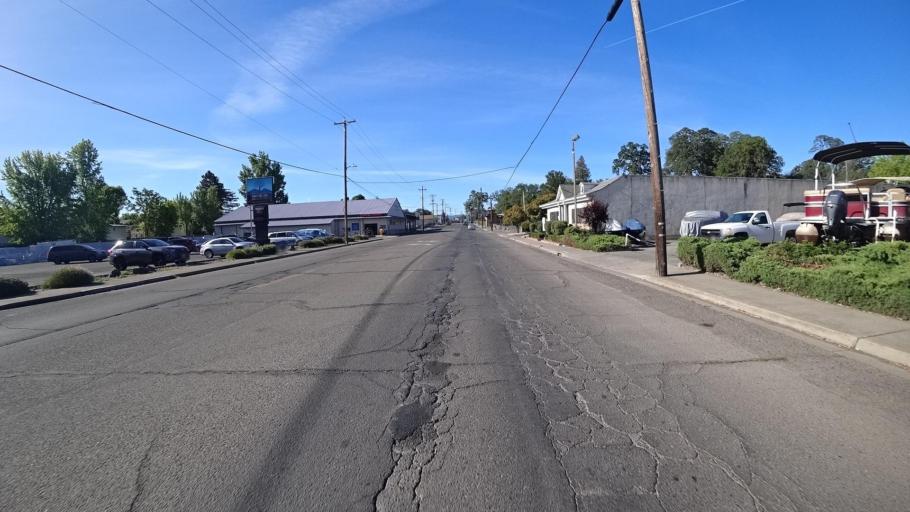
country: US
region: California
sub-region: Lake County
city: Lakeport
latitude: 39.0390
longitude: -122.9153
